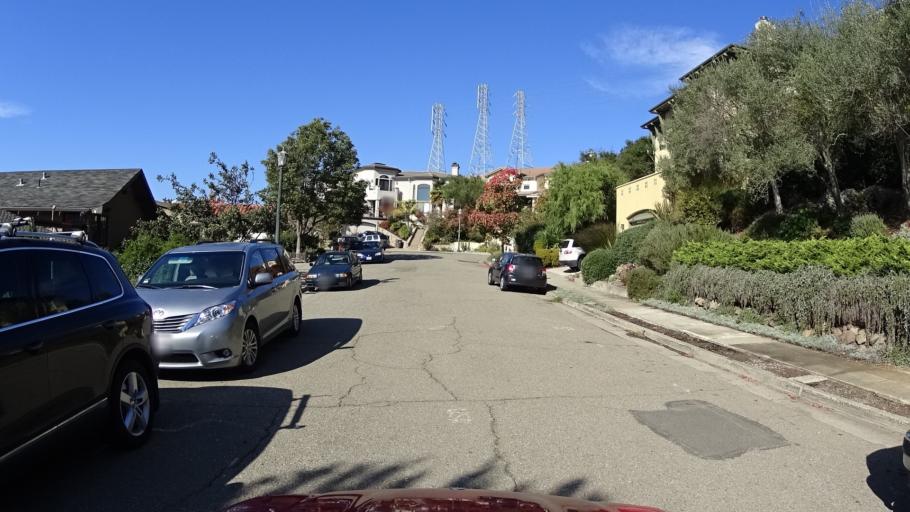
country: US
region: California
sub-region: Alameda County
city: Piedmont
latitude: 37.8460
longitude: -122.2249
